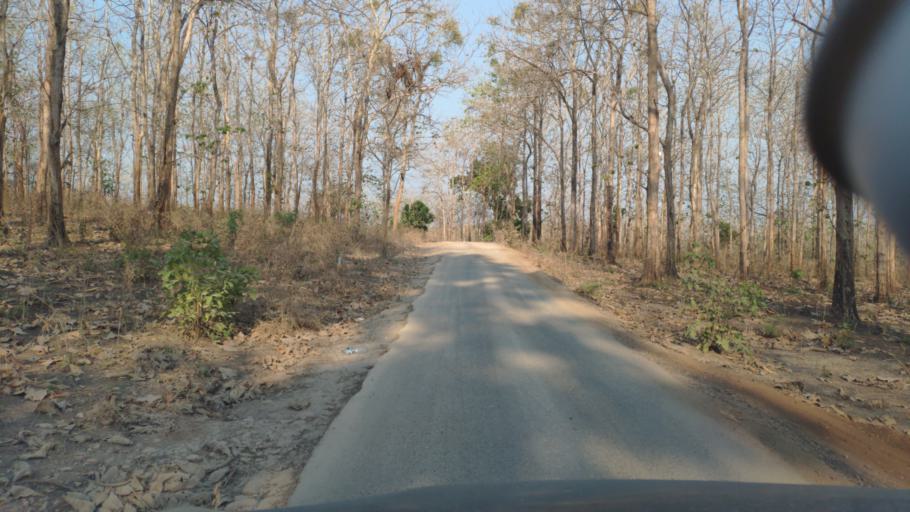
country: ID
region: Central Java
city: Sendangrejo
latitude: -6.9171
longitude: 111.5535
